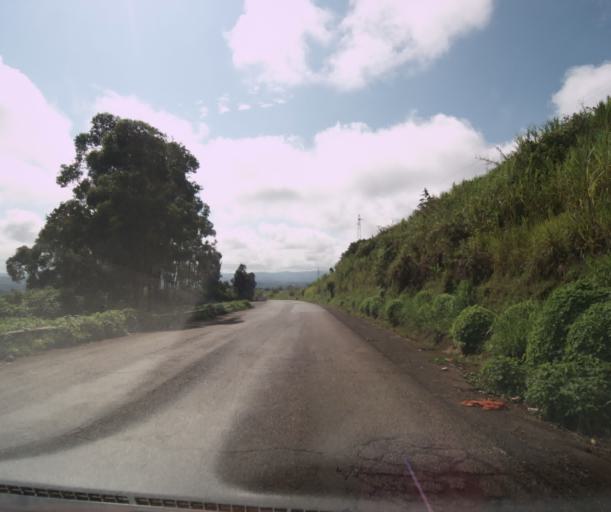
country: CM
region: West
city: Bafoussam
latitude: 5.4827
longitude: 10.4916
